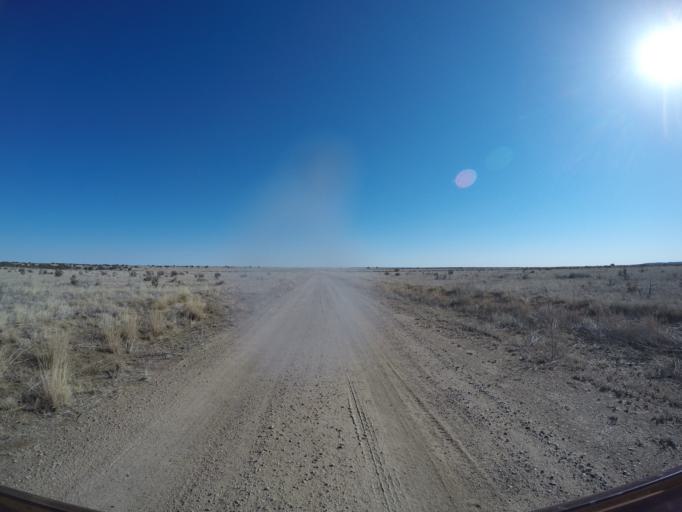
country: US
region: Colorado
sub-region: Otero County
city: La Junta
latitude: 37.6537
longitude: -103.6035
